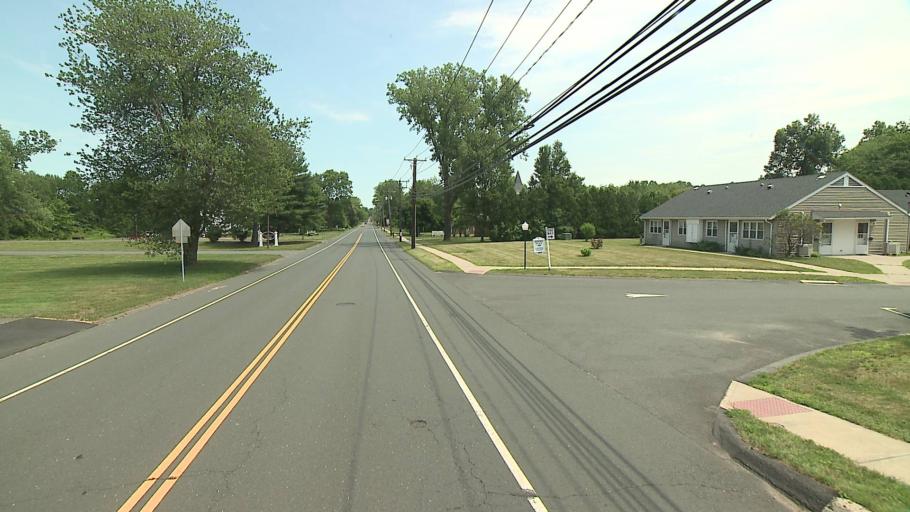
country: US
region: Connecticut
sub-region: Hartford County
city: Suffield Depot
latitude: 41.9805
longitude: -72.6467
